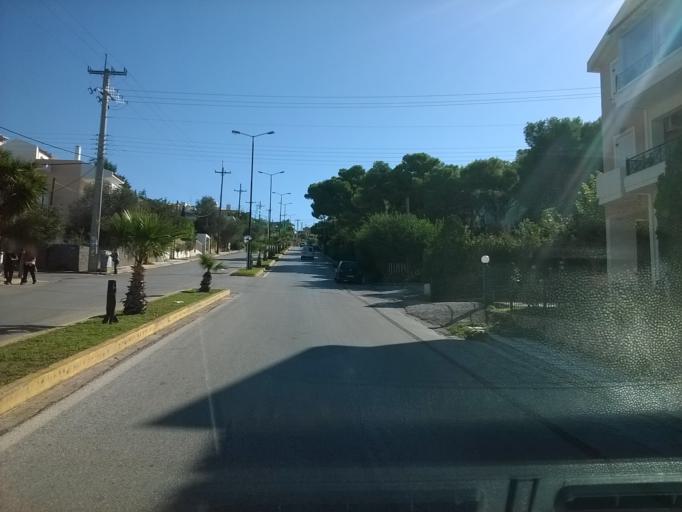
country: GR
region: Attica
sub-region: Nomarchia Anatolikis Attikis
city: Saronida
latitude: 37.7457
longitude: 23.9196
